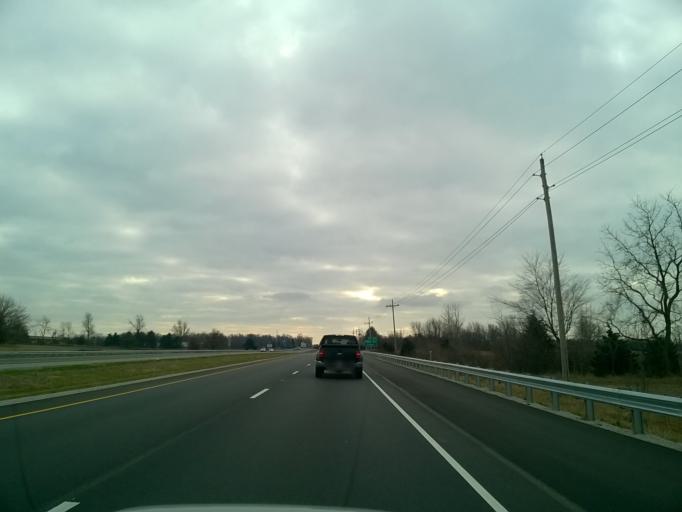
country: US
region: Indiana
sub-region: Hamilton County
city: Westfield
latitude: 40.0791
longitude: -86.1281
